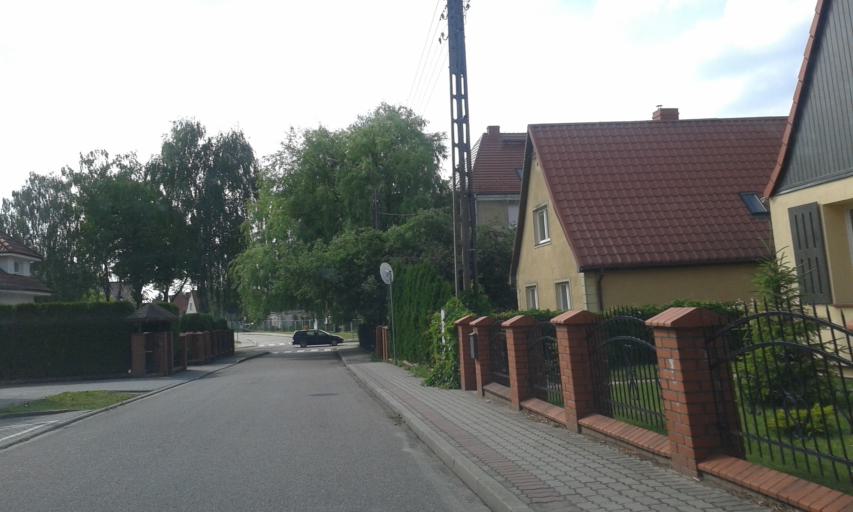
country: PL
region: West Pomeranian Voivodeship
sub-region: Powiat szczecinecki
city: Szczecinek
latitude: 53.7042
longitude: 16.7109
